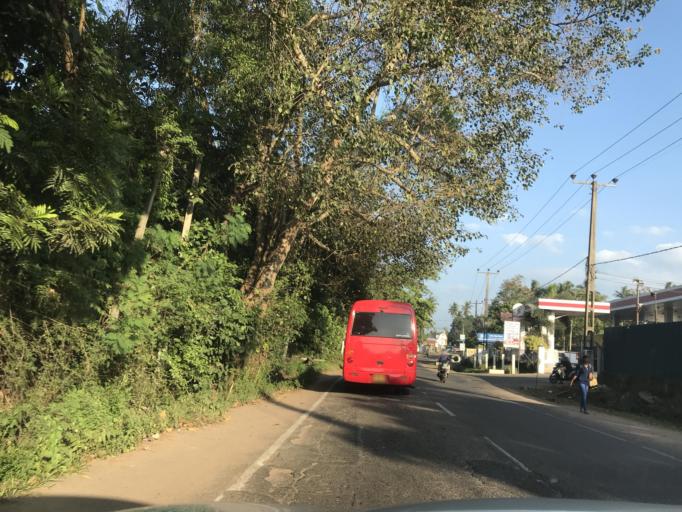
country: LK
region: Western
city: Ja Ela
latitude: 7.1013
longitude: 79.9125
